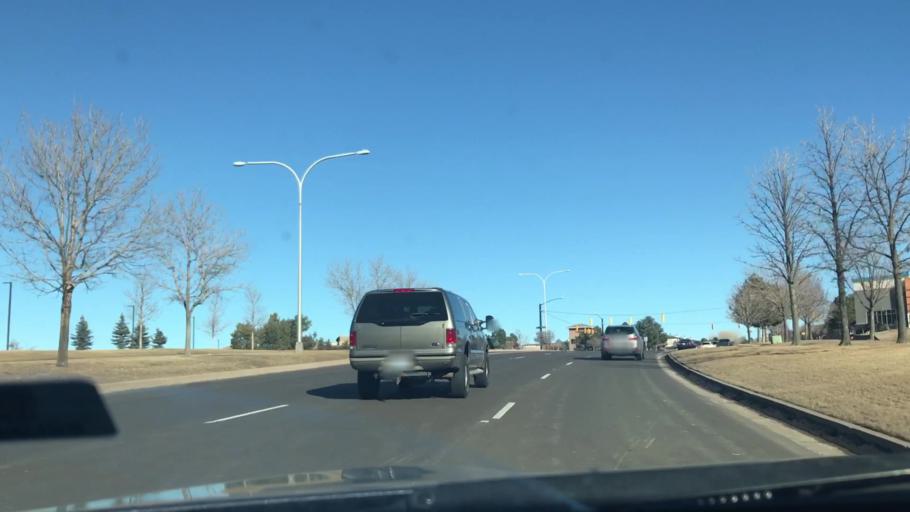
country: US
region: Colorado
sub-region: El Paso County
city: Air Force Academy
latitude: 38.9664
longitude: -104.7868
